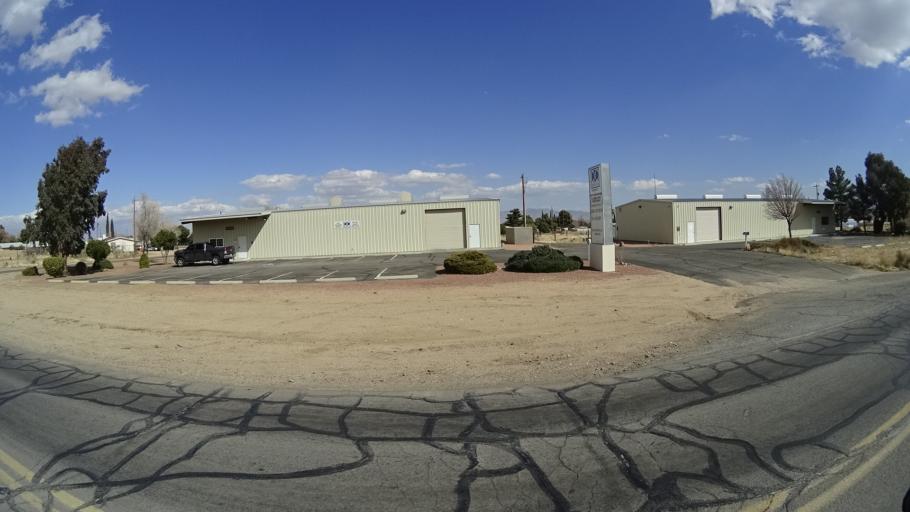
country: US
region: Arizona
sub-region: Mohave County
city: New Kingman-Butler
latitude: 35.2652
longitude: -114.0416
